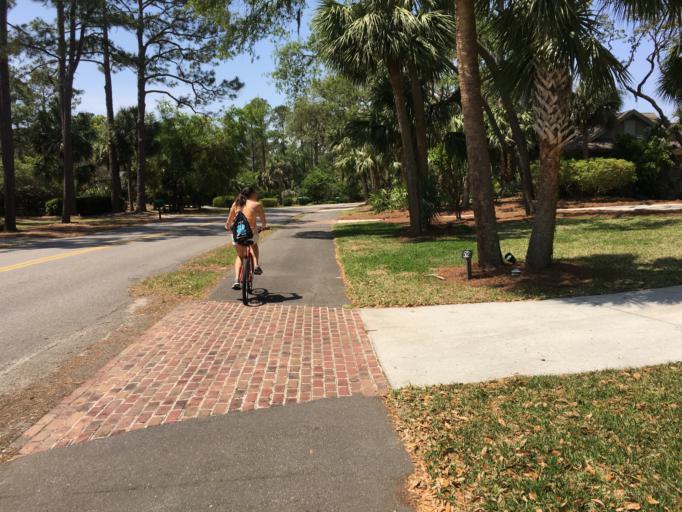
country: US
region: Georgia
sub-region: Chatham County
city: Tybee Island
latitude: 32.1136
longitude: -80.8132
